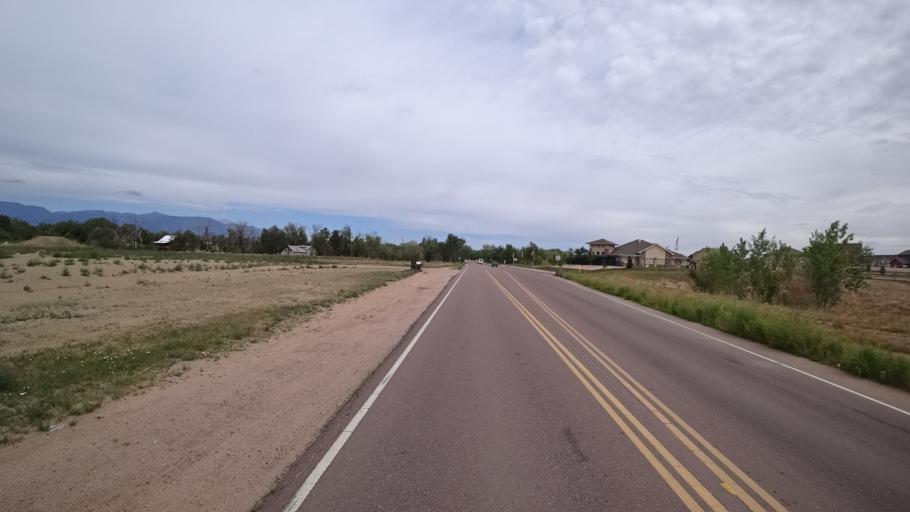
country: US
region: Colorado
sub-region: El Paso County
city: Fountain
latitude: 38.6704
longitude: -104.6952
